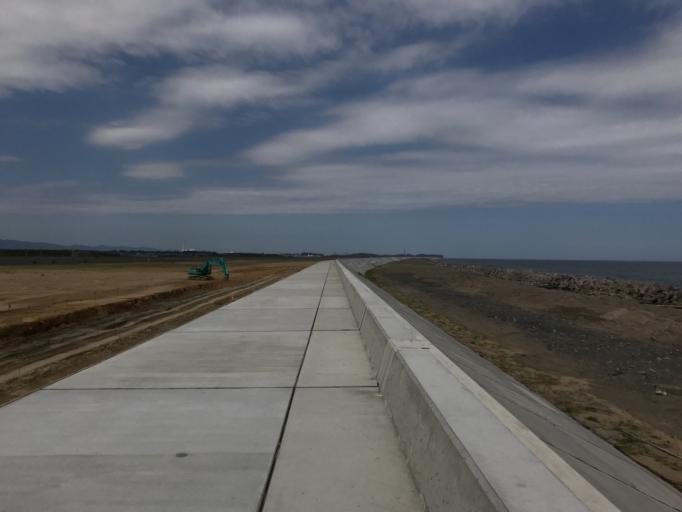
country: JP
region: Miyagi
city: Marumori
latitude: 37.7754
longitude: 140.9880
